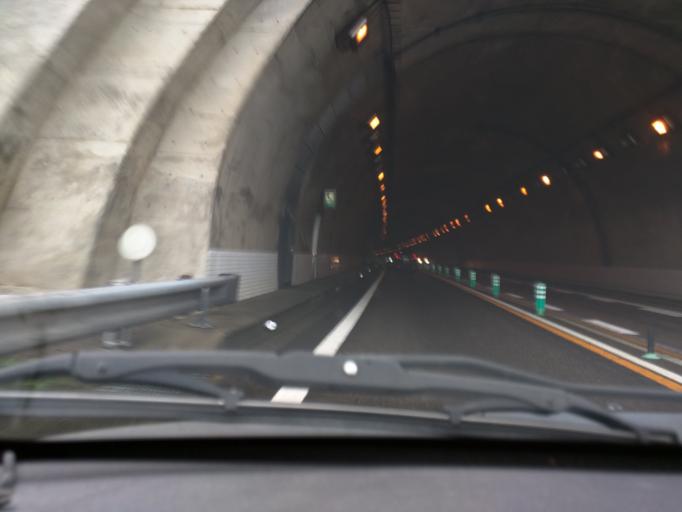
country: JP
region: Niigata
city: Joetsu
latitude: 37.1061
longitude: 138.2199
